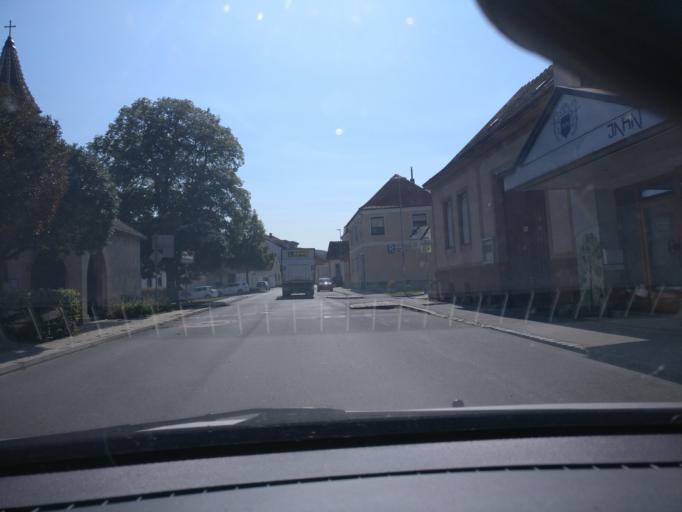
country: AT
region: Burgenland
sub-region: Politischer Bezirk Mattersburg
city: Mattersburg
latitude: 47.7361
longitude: 16.3949
